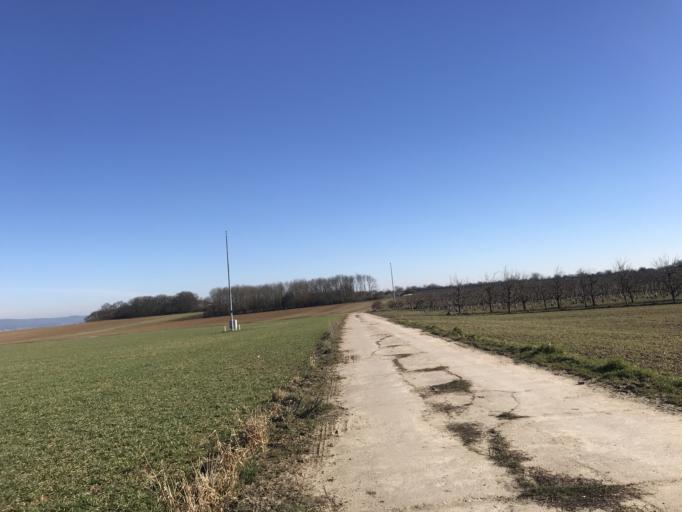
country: DE
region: Rheinland-Pfalz
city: Wackernheim
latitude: 49.9664
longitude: 8.1343
